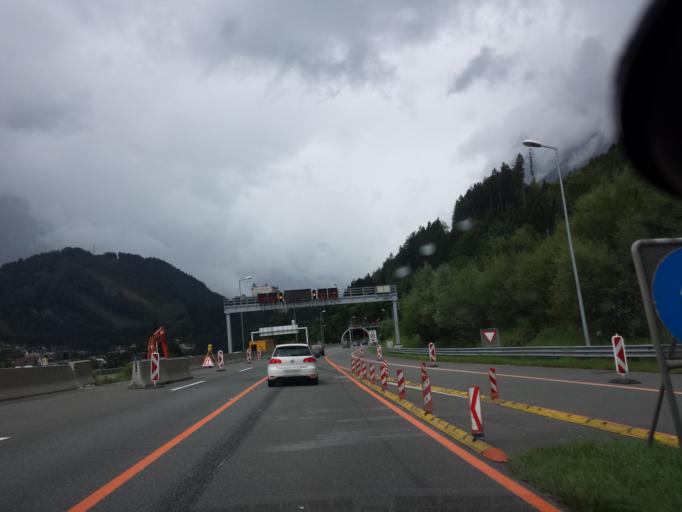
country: AT
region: Salzburg
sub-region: Politischer Bezirk Sankt Johann im Pongau
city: Pfarrwerfen
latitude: 47.4700
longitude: 13.1997
